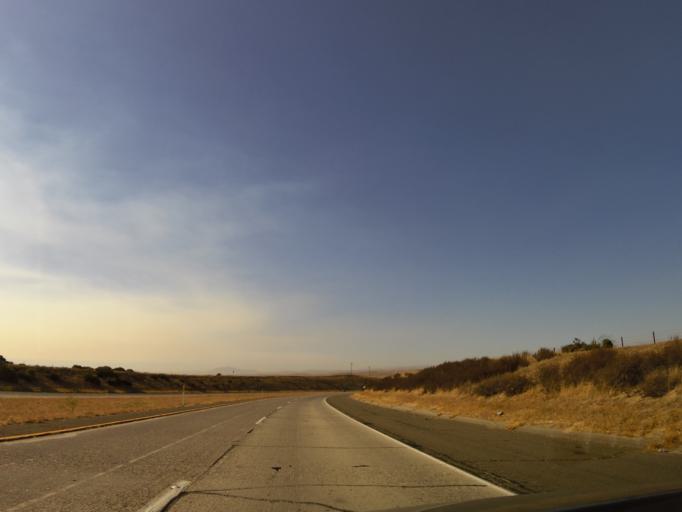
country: US
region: California
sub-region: Monterey County
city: King City
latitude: 36.0983
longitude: -121.0246
